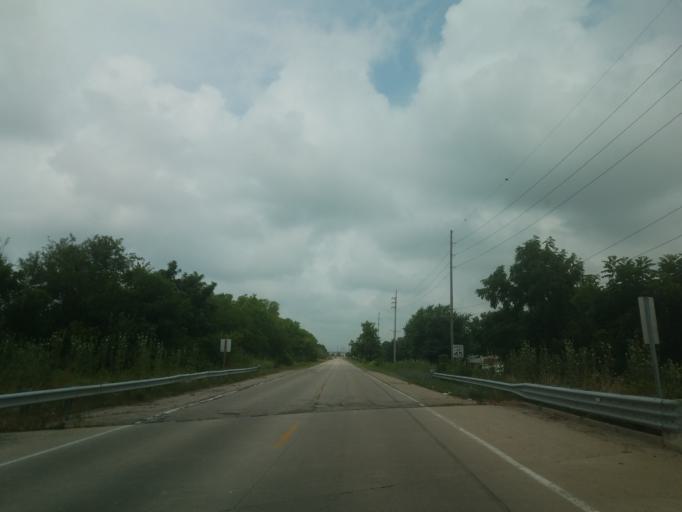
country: US
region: Illinois
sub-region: McLean County
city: Bloomington
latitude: 40.4889
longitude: -89.0162
